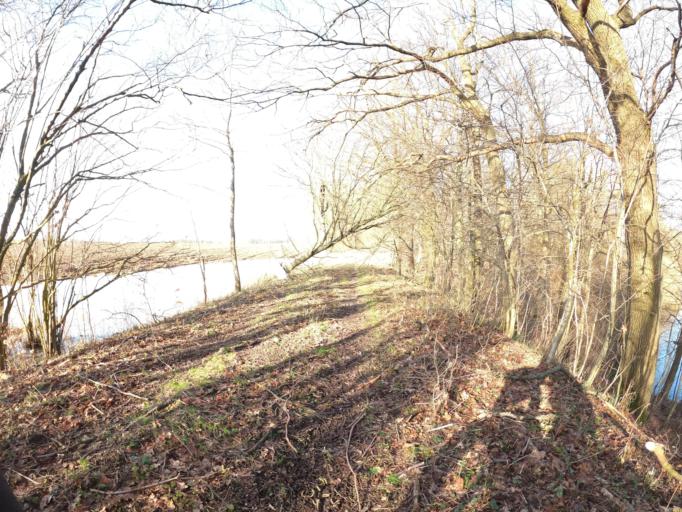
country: PL
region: West Pomeranian Voivodeship
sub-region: Powiat koszalinski
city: Polanow
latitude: 54.1465
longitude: 16.7668
